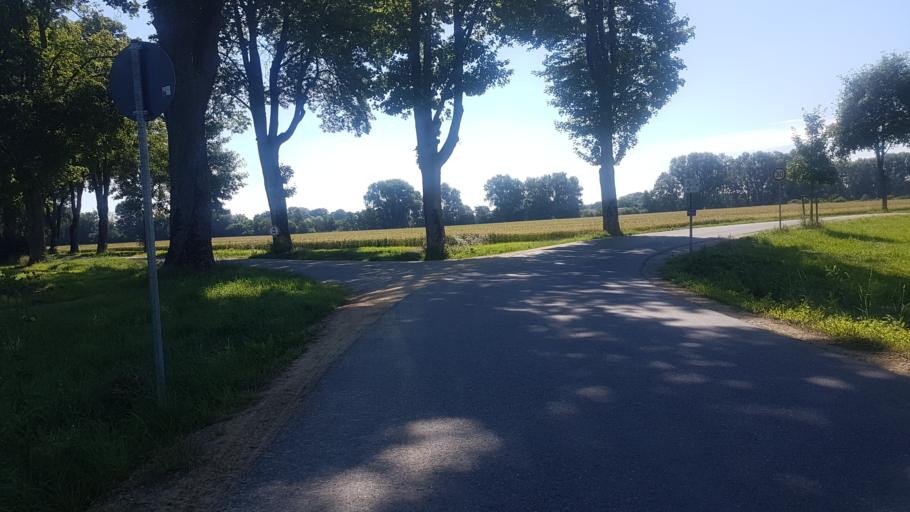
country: DE
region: Bavaria
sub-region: Upper Bavaria
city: Bergheim
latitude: 48.7257
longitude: 11.2794
